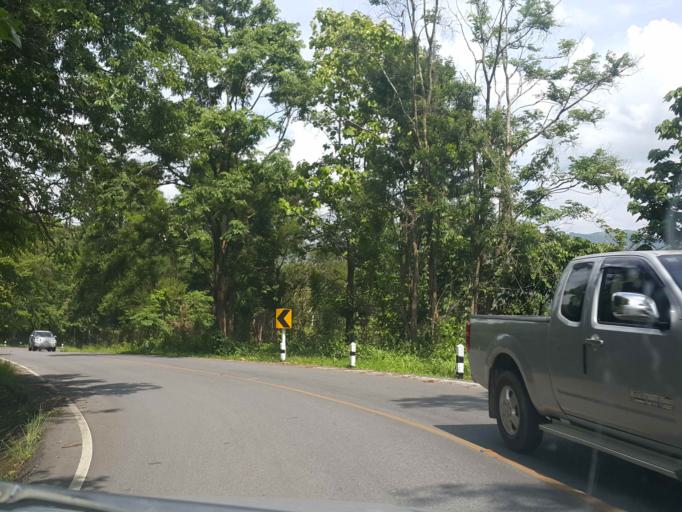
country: TH
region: Nan
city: Ban Luang
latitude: 18.8759
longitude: 100.5432
